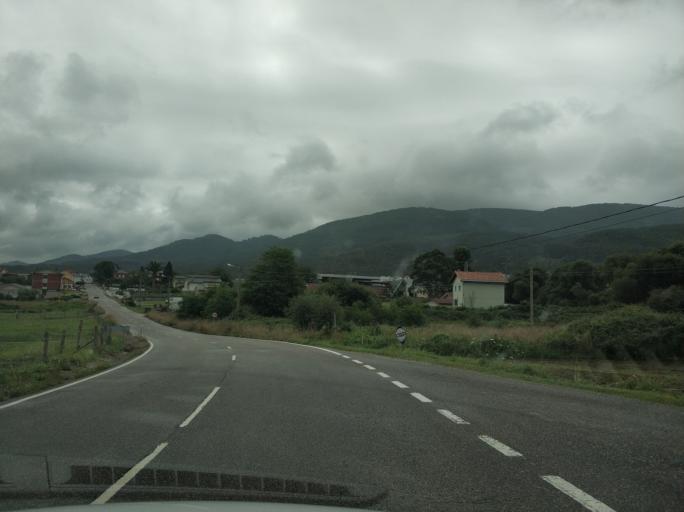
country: ES
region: Asturias
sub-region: Province of Asturias
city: Salas
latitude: 43.5449
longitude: -6.3938
